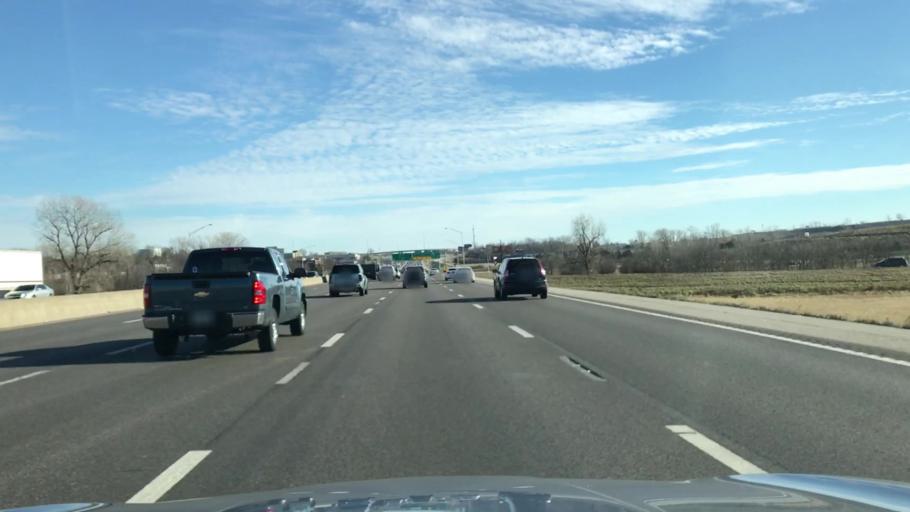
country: US
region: Missouri
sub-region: Saint Charles County
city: Saint Charles
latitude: 38.7567
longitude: -90.4620
